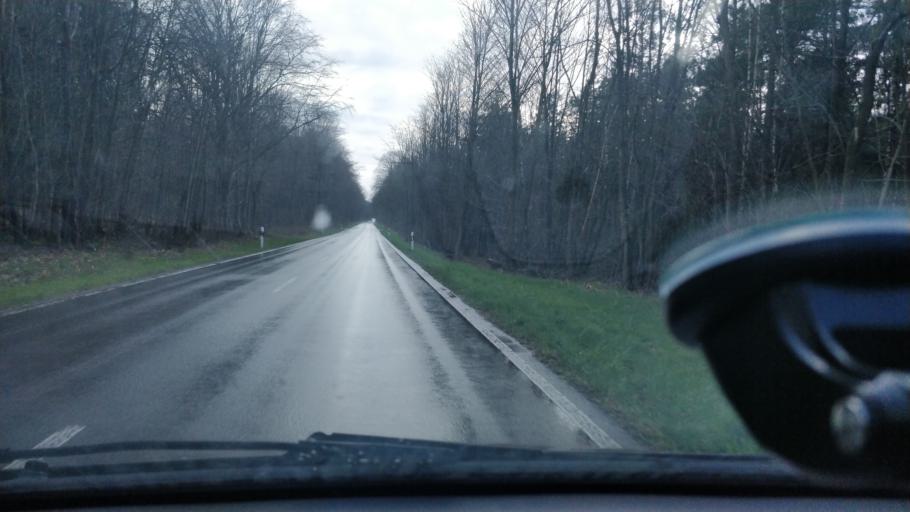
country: DE
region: North Rhine-Westphalia
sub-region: Regierungsbezirk Dusseldorf
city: Uedem
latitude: 51.6843
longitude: 6.3529
